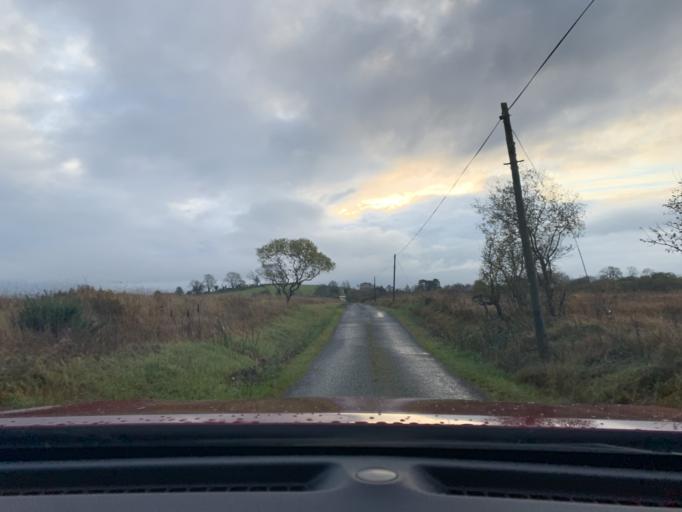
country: IE
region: Connaught
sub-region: Sligo
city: Ballymote
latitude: 54.0306
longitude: -8.5278
